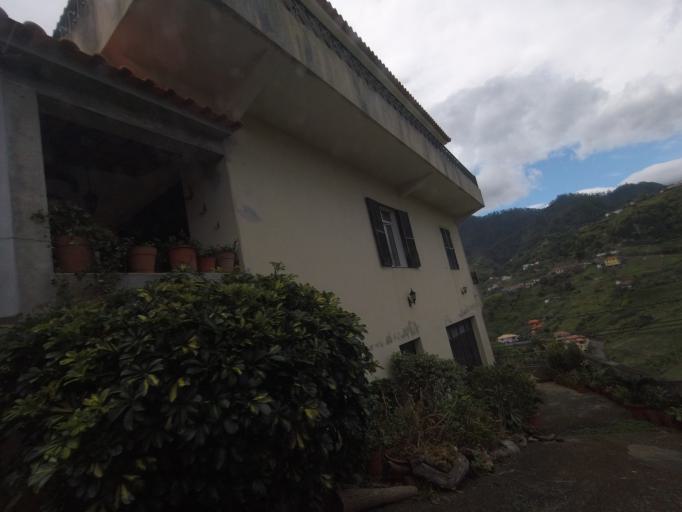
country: PT
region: Madeira
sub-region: Santana
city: Santana
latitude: 32.7677
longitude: -16.8266
